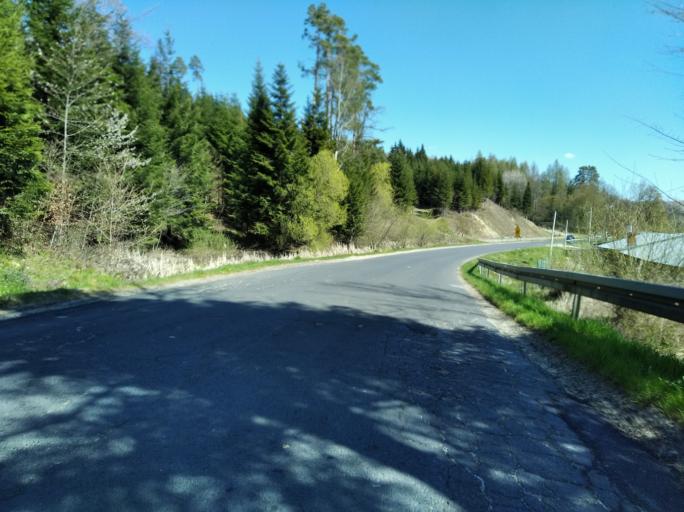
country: PL
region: Subcarpathian Voivodeship
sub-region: Powiat brzozowski
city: Dydnia
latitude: 49.7119
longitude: 22.2019
